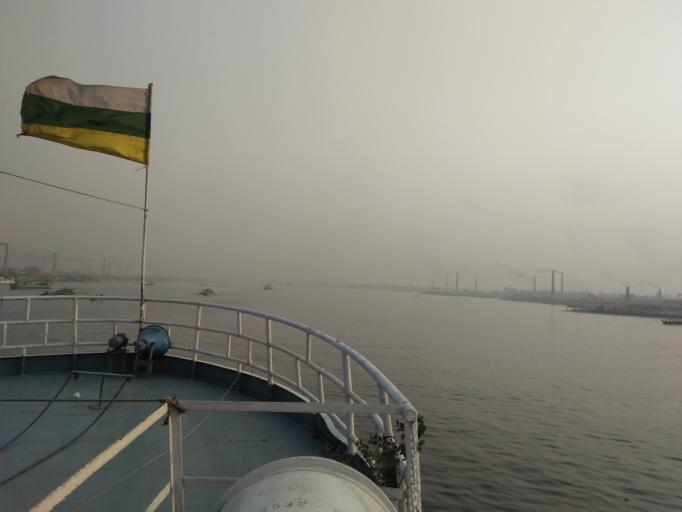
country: BD
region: Dhaka
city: Narayanganj
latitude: 23.6231
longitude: 90.4533
